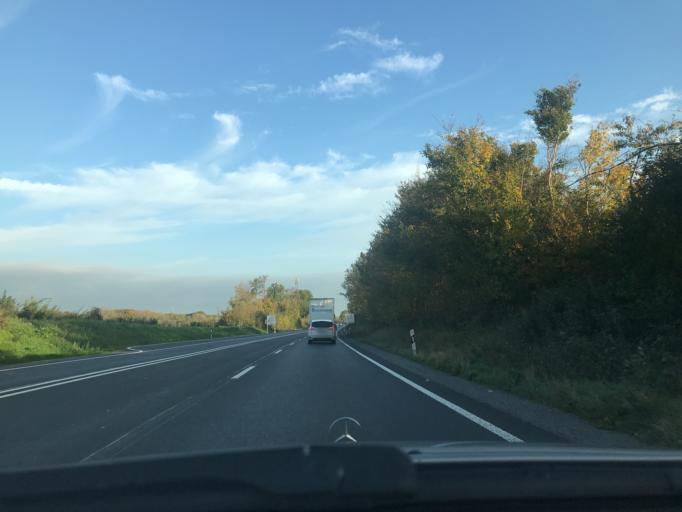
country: DE
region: North Rhine-Westphalia
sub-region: Regierungsbezirk Arnsberg
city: Soest
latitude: 51.5671
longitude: 8.1380
